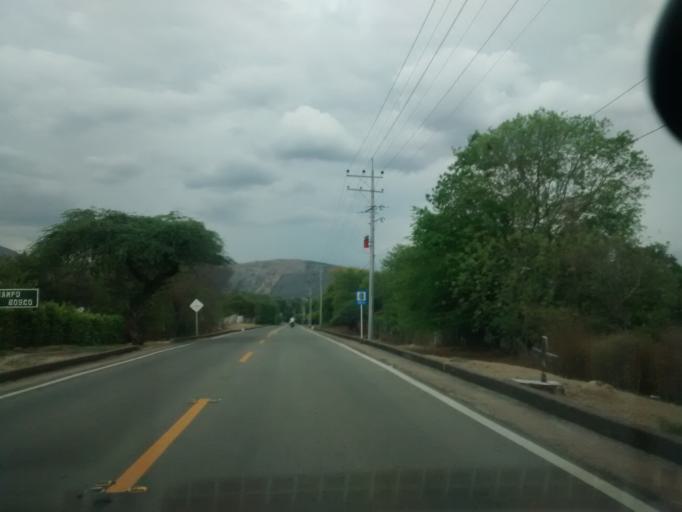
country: CO
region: Cundinamarca
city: Tocaima
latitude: 4.4503
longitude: -74.6531
